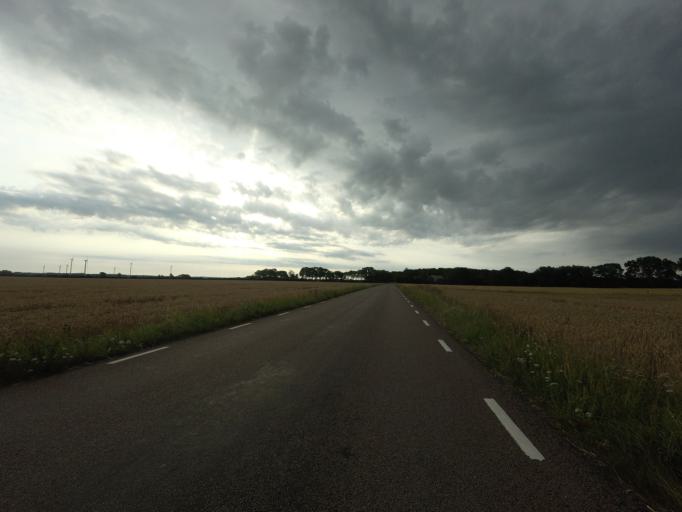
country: SE
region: Skane
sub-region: Helsingborg
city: Odakra
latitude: 56.1533
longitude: 12.7272
